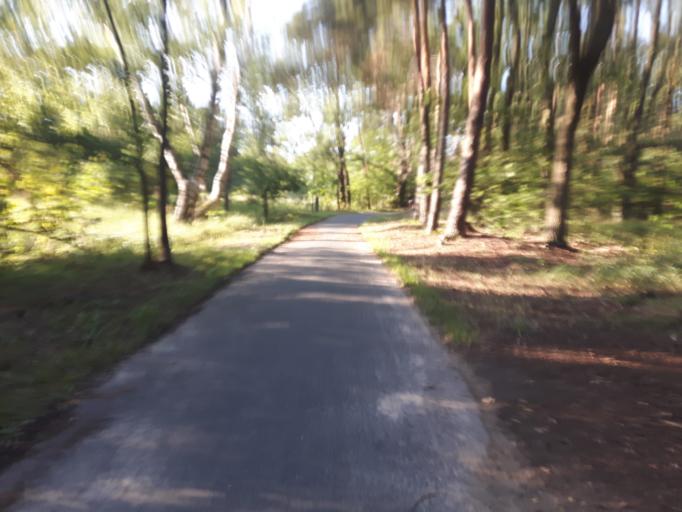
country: DE
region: Berlin
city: Falkenhagener Feld
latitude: 52.5639
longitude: 13.1475
